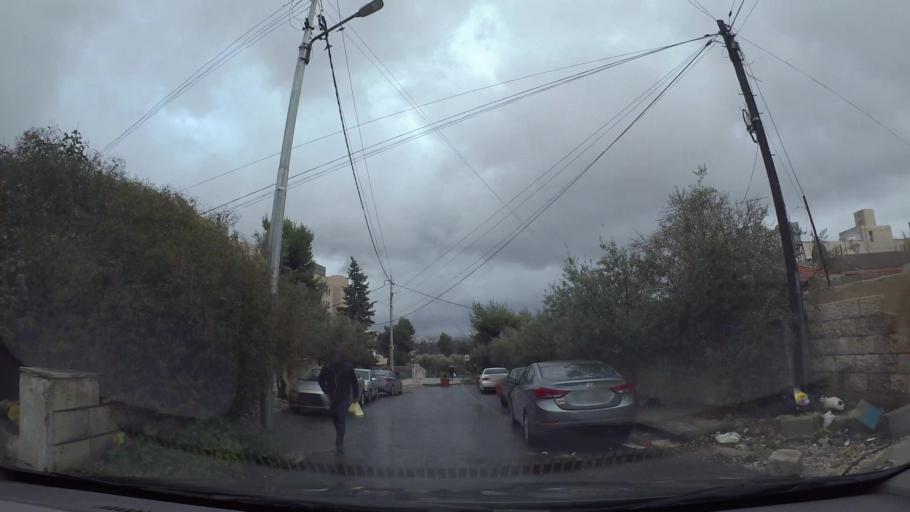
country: JO
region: Amman
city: Al Jubayhah
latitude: 32.0199
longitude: 35.8675
